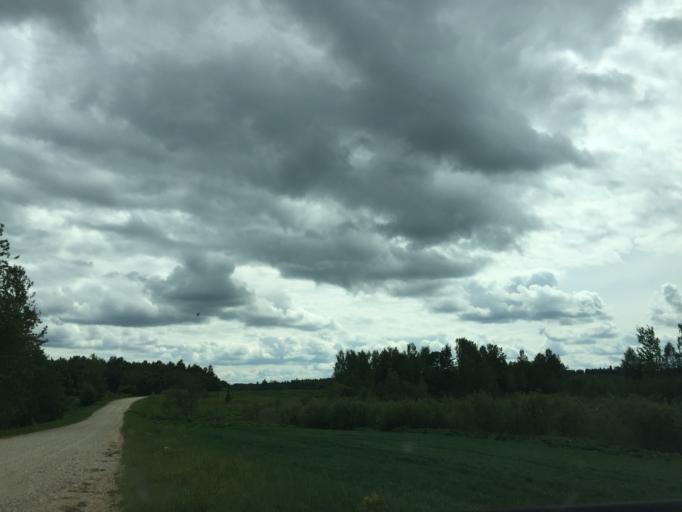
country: LV
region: Dagda
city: Dagda
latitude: 56.0648
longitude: 27.6500
